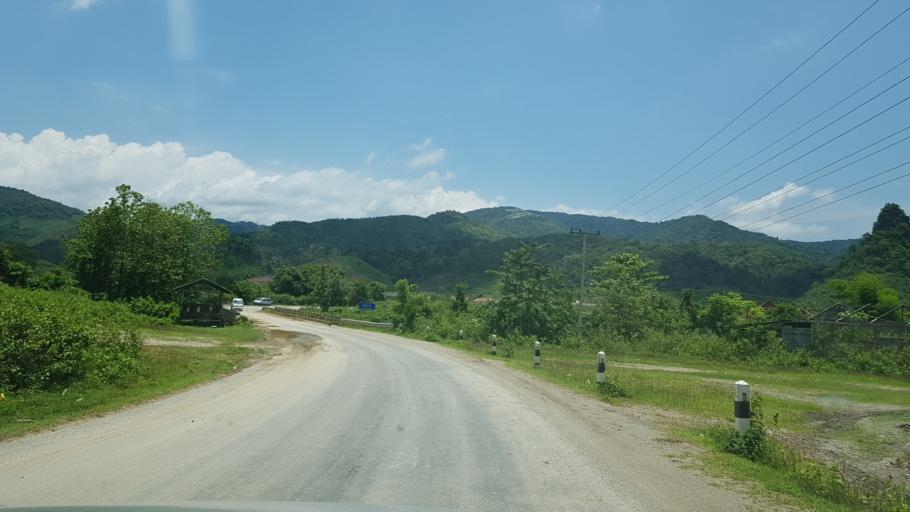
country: LA
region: Vientiane
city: Muang Kasi
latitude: 19.2737
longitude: 102.2169
